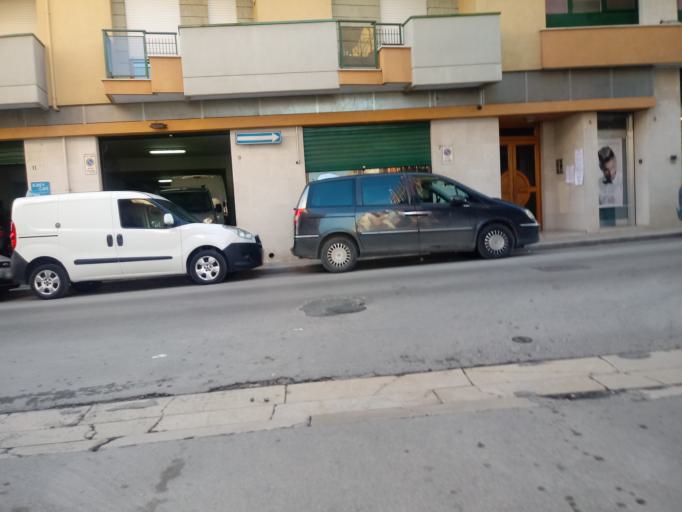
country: IT
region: Apulia
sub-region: Provincia di Barletta - Andria - Trani
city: Andria
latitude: 41.2190
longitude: 16.2943
